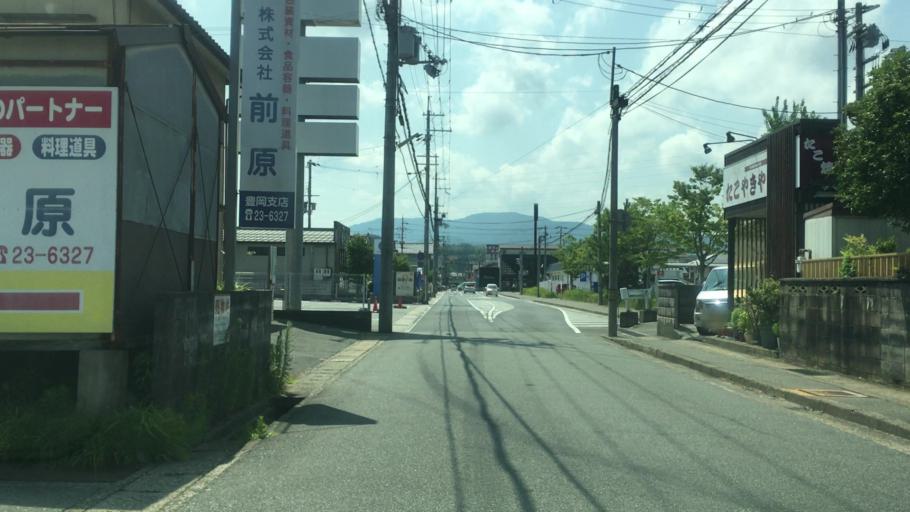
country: JP
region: Hyogo
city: Toyooka
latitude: 35.5490
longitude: 134.8173
